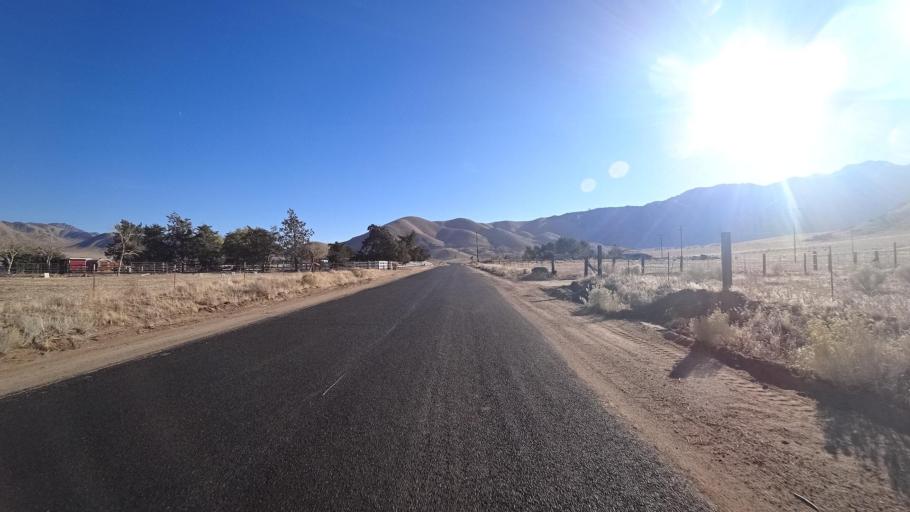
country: US
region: California
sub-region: Kern County
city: Weldon
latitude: 35.6271
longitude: -118.2642
